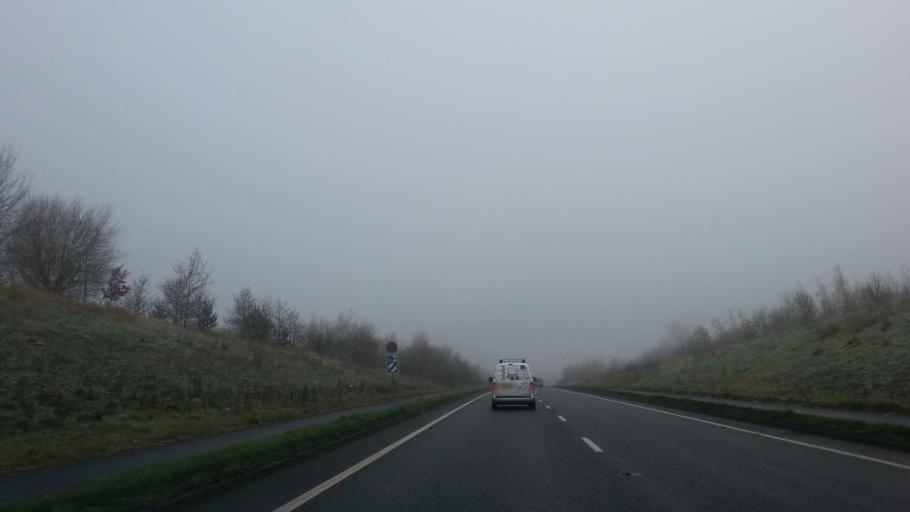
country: GB
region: England
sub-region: Cheshire East
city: Alderley Edge
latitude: 53.3006
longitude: -2.2496
